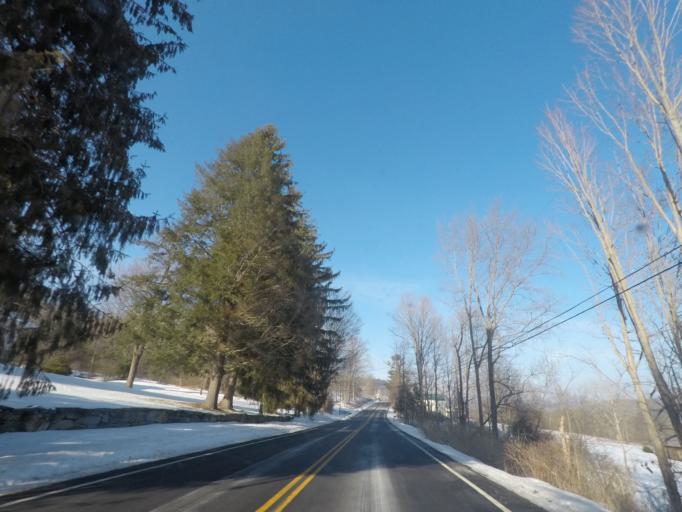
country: US
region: Massachusetts
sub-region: Berkshire County
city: Richmond
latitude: 42.4893
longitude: -73.3880
